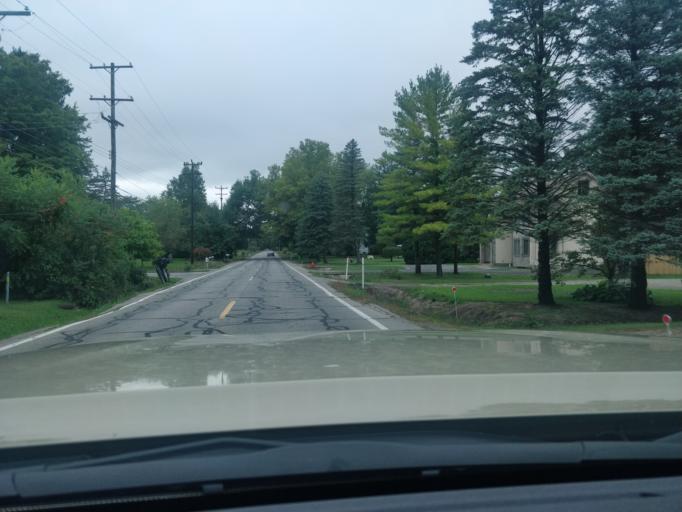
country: US
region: Michigan
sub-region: Wayne County
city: Romulus
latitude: 42.2038
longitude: -83.4239
